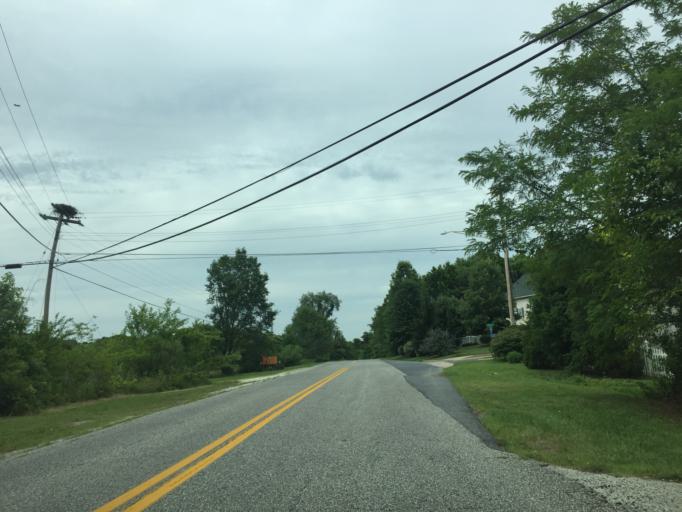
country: US
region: Maryland
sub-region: Baltimore County
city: Edgemere
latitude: 39.2575
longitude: -76.4554
